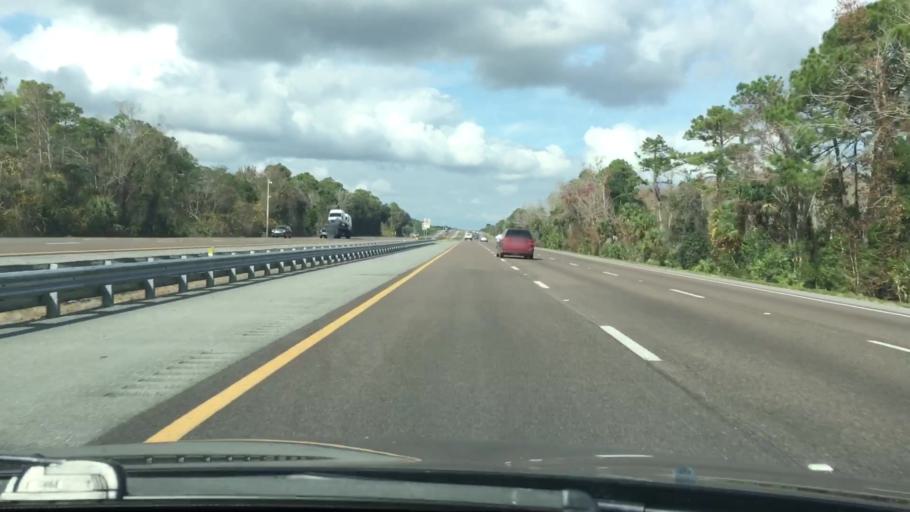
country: US
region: Florida
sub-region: Volusia County
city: Oak Hill
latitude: 28.8234
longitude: -80.9089
